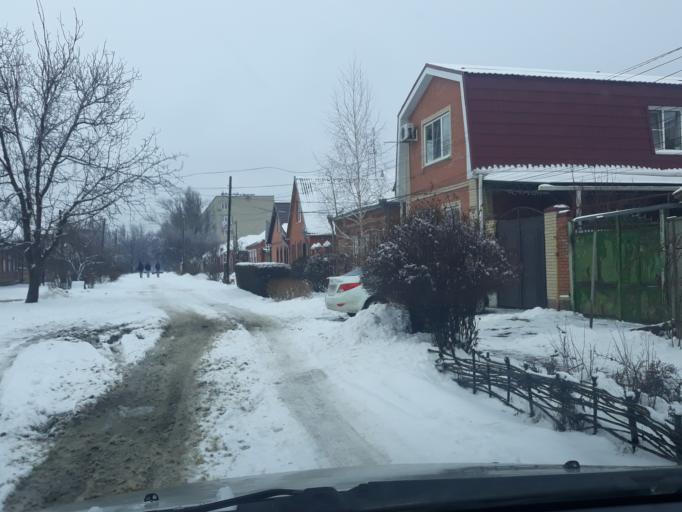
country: RU
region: Rostov
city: Taganrog
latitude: 47.2302
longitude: 38.8778
